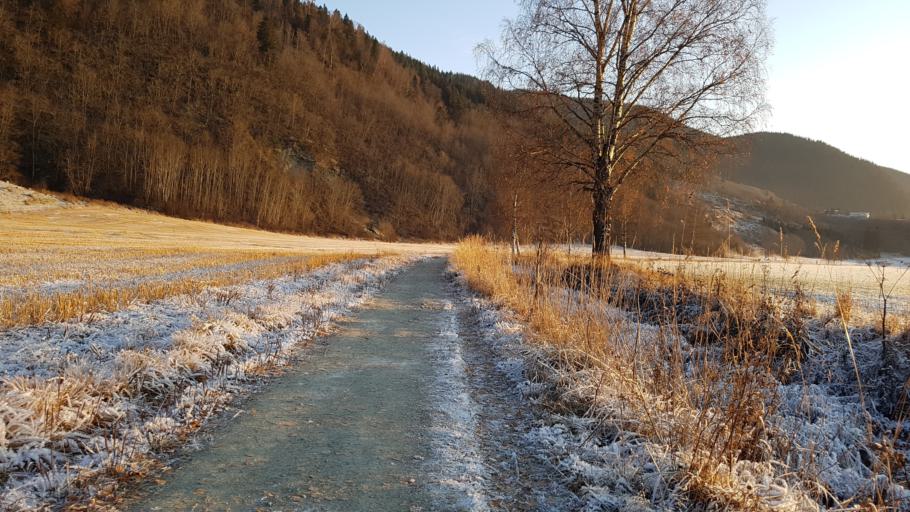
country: NO
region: Sor-Trondelag
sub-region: Melhus
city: Melhus
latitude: 63.2826
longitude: 10.2998
